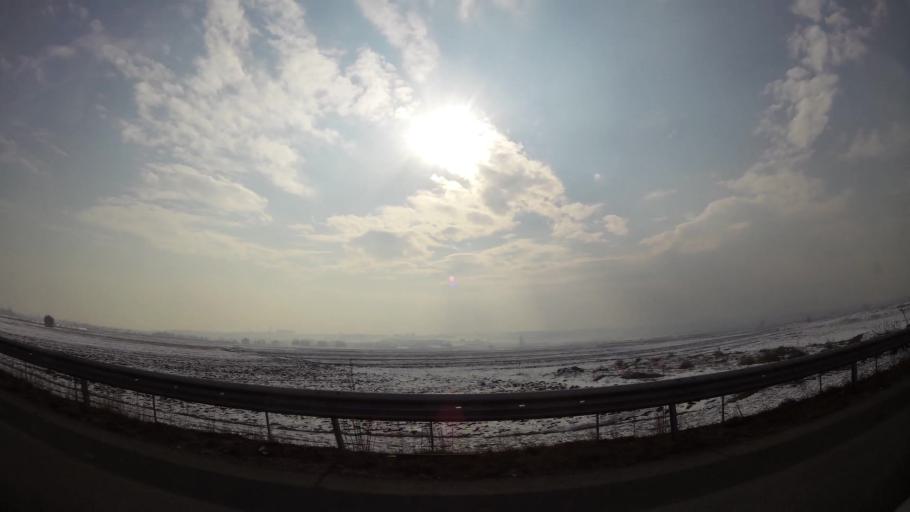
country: MK
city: Creshevo
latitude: 42.0313
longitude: 21.5023
